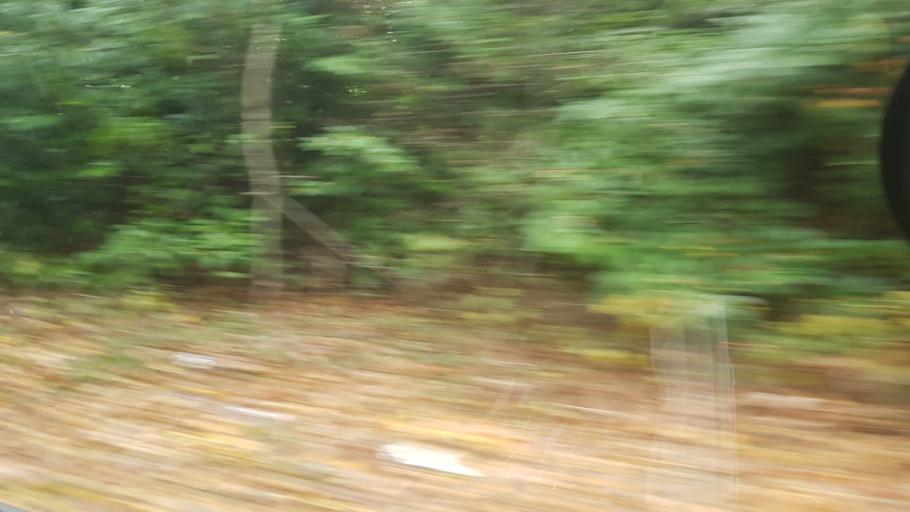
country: GB
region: England
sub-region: Hampshire
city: Aldershot
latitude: 51.2511
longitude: -0.7797
